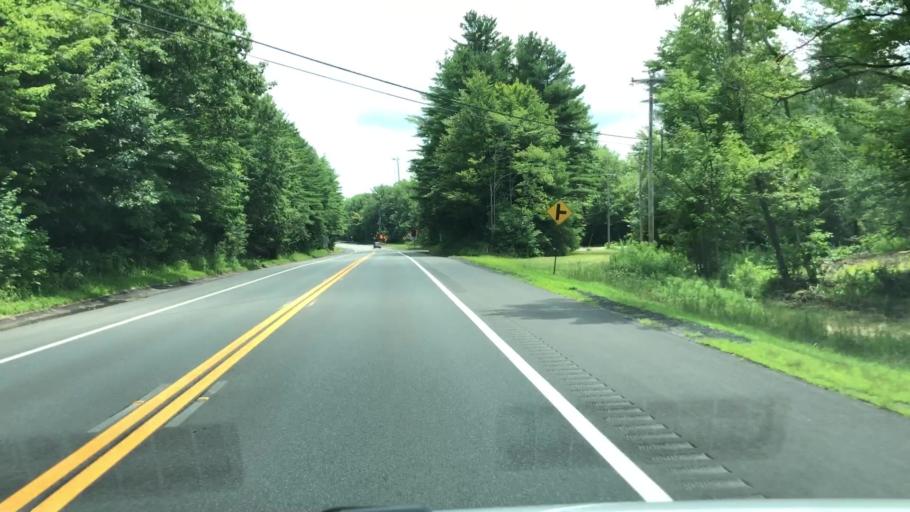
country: US
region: Massachusetts
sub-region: Hampshire County
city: Chesterfield
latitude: 42.4477
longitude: -72.8103
